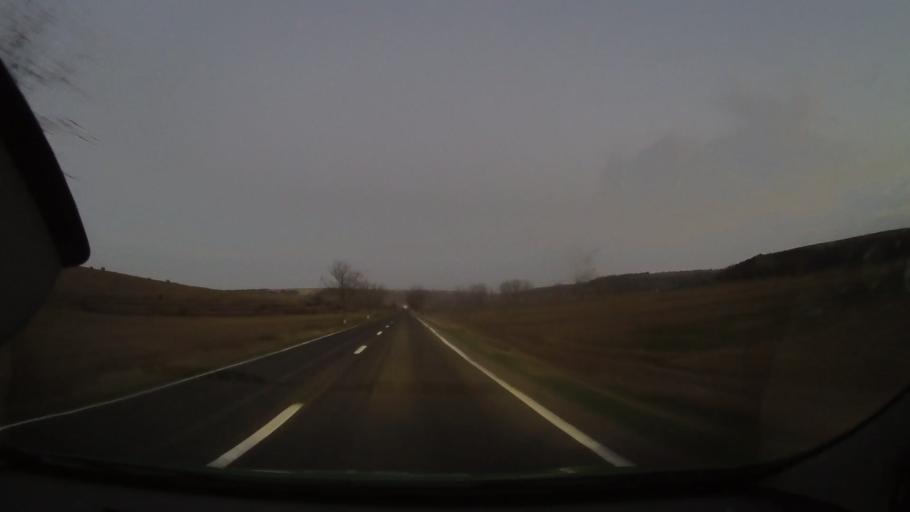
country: RO
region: Constanta
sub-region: Comuna Ion Corvin
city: Ion Corvin
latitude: 44.1032
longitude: 27.7888
